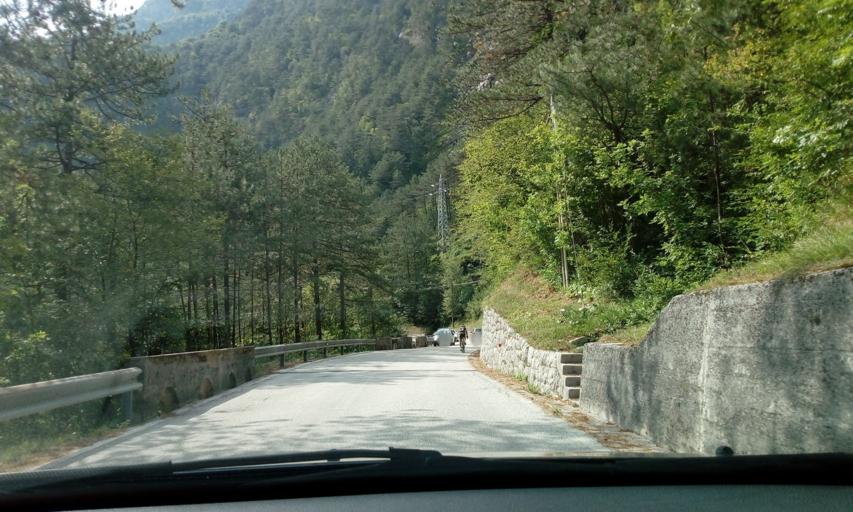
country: IT
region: Friuli Venezia Giulia
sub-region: Provincia di Udine
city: Chiusaforte
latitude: 46.4010
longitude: 13.3189
